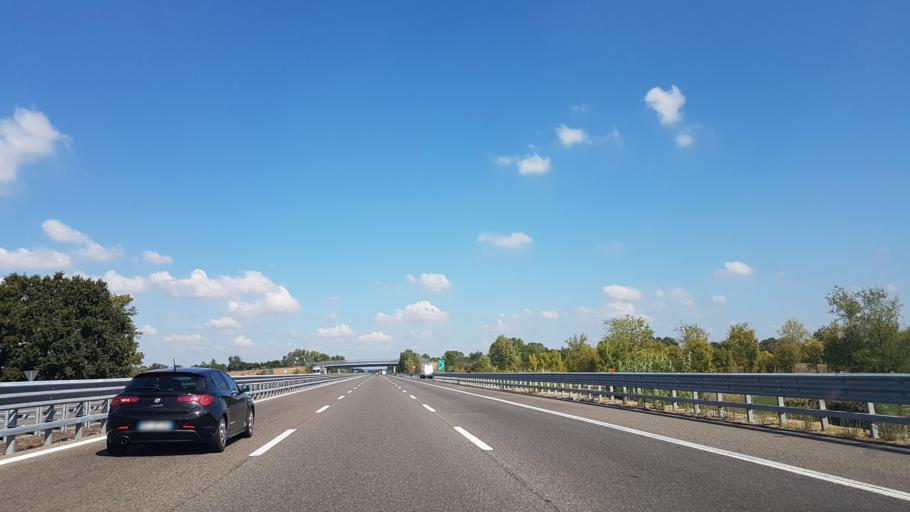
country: IT
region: Piedmont
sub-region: Provincia di Alessandria
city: Castelnuovo Scrivia
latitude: 44.9587
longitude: 8.8778
